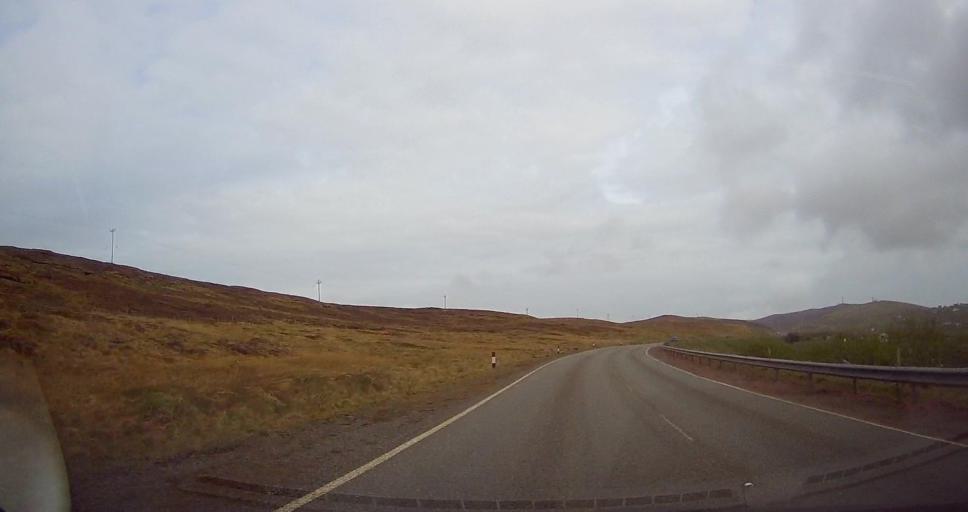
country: GB
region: Scotland
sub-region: Shetland Islands
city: Lerwick
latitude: 60.1234
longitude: -1.2169
